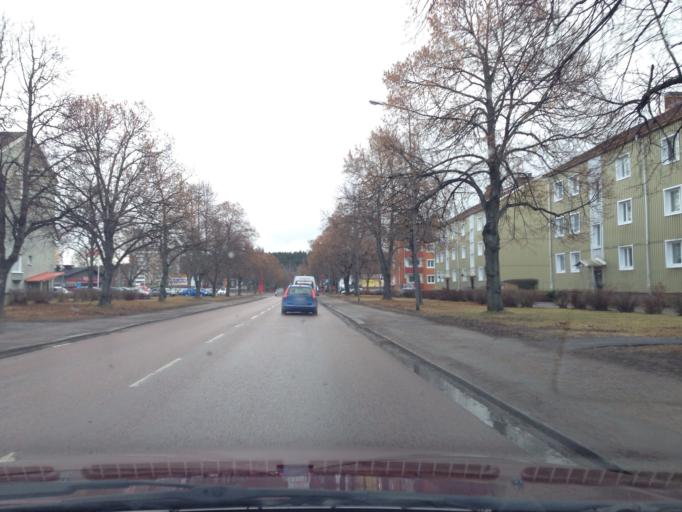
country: SE
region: Dalarna
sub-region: Ludvika Kommun
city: Ludvika
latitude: 60.1502
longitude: 15.2043
